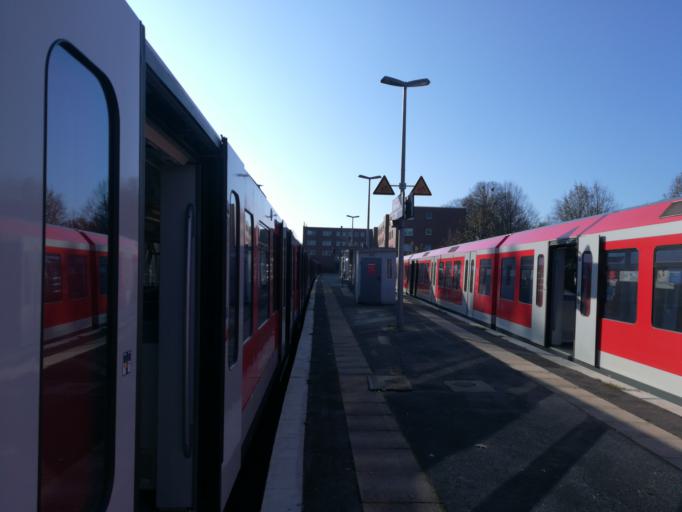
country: DE
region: Schleswig-Holstein
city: Wedel
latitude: 53.5827
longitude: 9.7062
